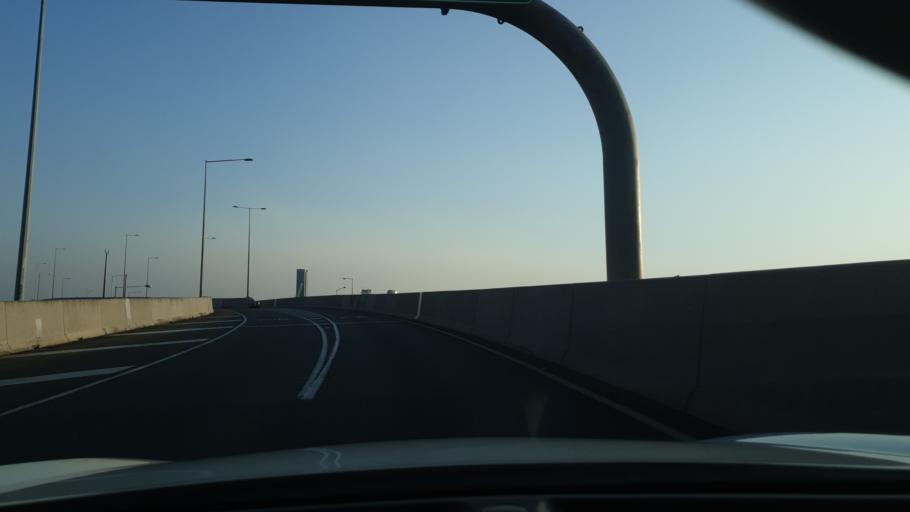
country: AU
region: Queensland
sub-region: Brisbane
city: Windsor
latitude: -27.4431
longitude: 153.0322
